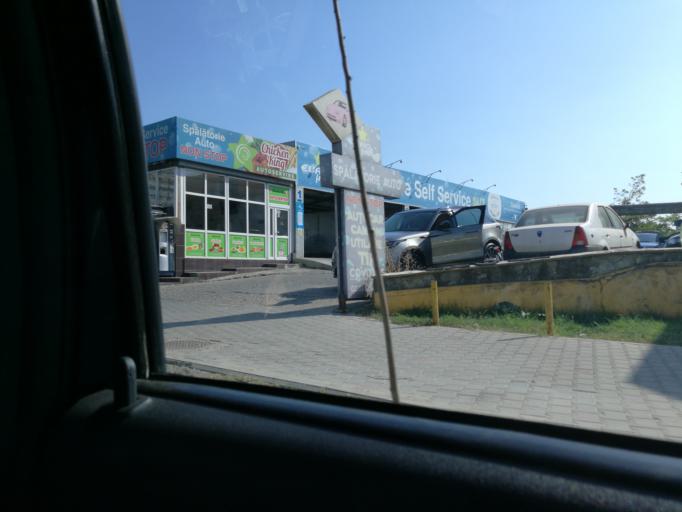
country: RO
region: Iasi
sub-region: Municipiul Iasi
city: Iasi
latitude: 47.1717
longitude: 27.5598
